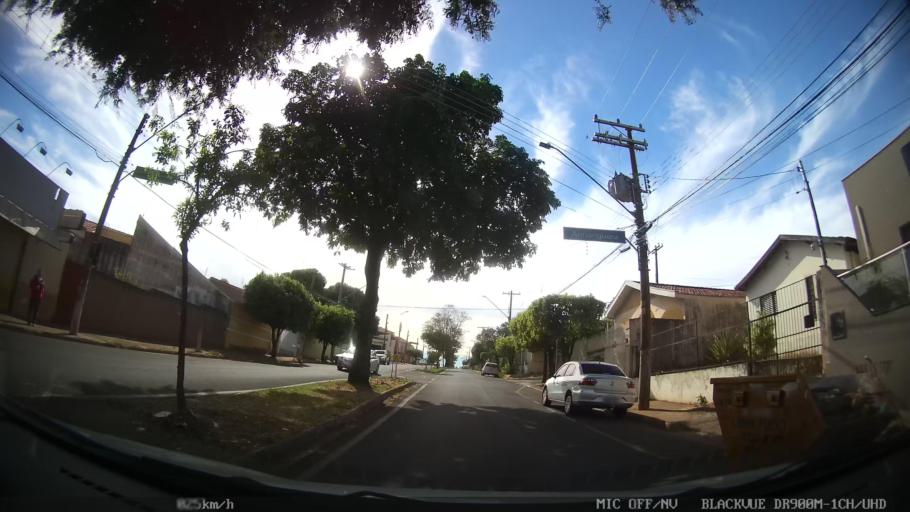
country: BR
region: Sao Paulo
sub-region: Catanduva
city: Catanduva
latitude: -21.1258
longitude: -48.9493
